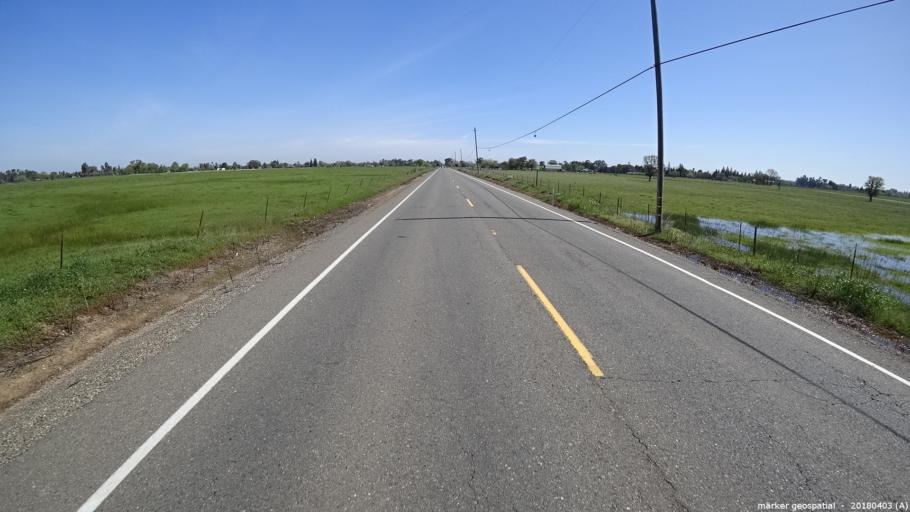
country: US
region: California
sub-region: Sacramento County
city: Wilton
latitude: 38.3877
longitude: -121.2802
